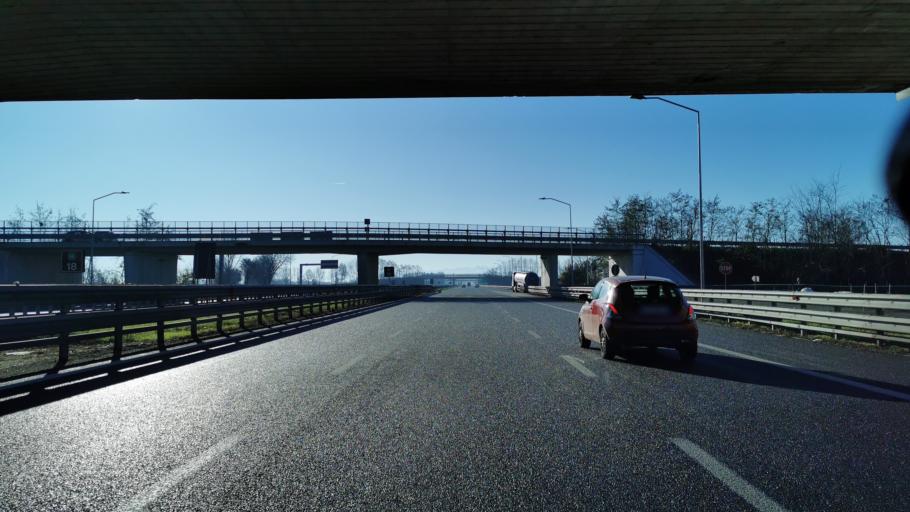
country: IT
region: Piedmont
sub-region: Provincia di Torino
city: Carmagnola
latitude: 44.8523
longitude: 7.7486
